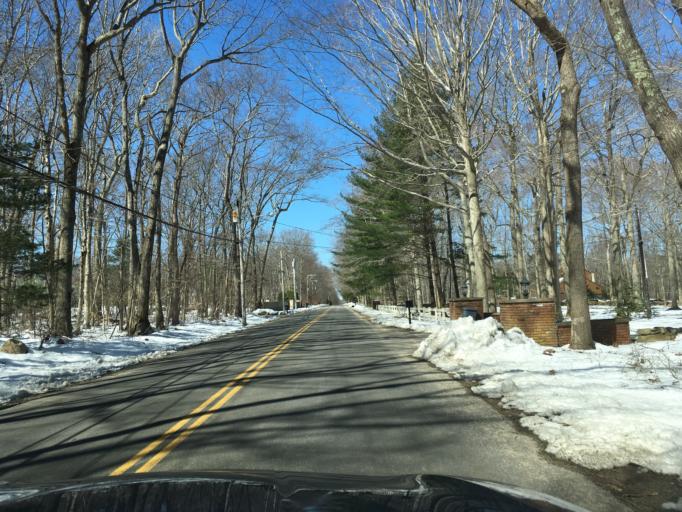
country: US
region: Rhode Island
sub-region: Washington County
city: Exeter
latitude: 41.6083
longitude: -71.5348
